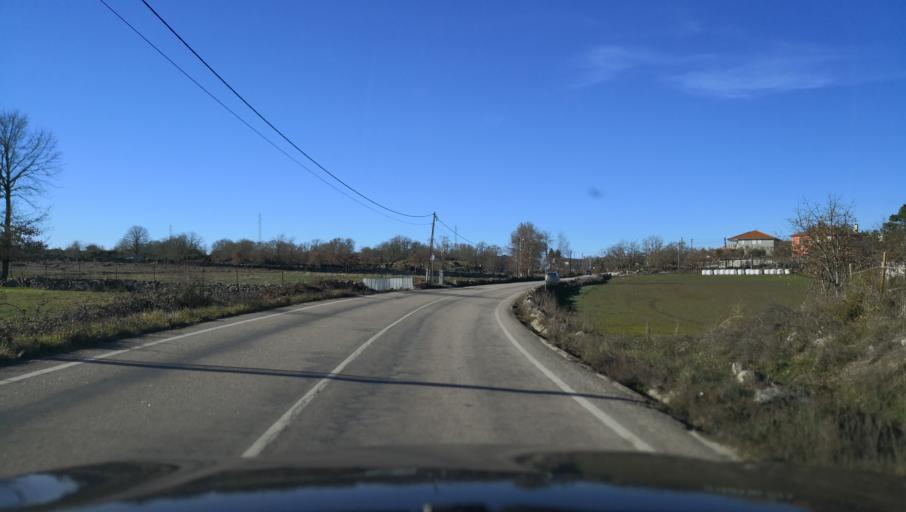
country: PT
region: Vila Real
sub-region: Vila Pouca de Aguiar
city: Vila Pouca de Aguiar
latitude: 41.4972
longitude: -7.6805
